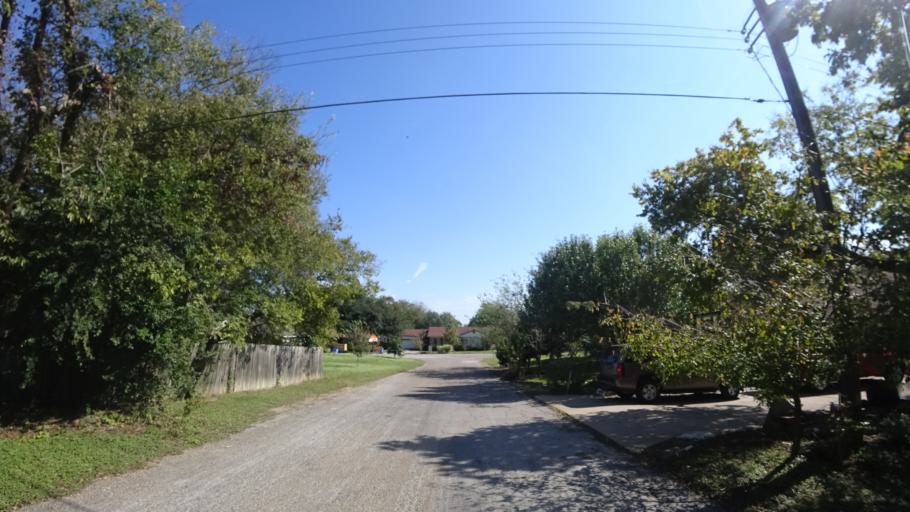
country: US
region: Texas
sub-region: Travis County
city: Pflugerville
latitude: 30.4192
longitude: -97.6243
